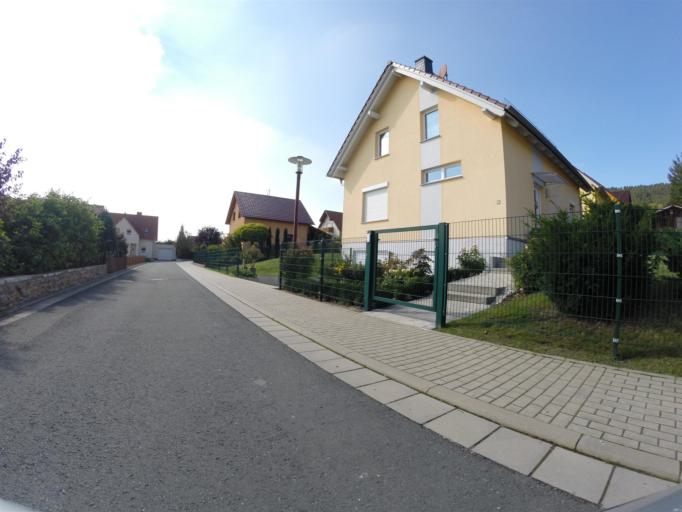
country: DE
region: Thuringia
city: Zollnitz
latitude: 50.8894
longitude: 11.6299
